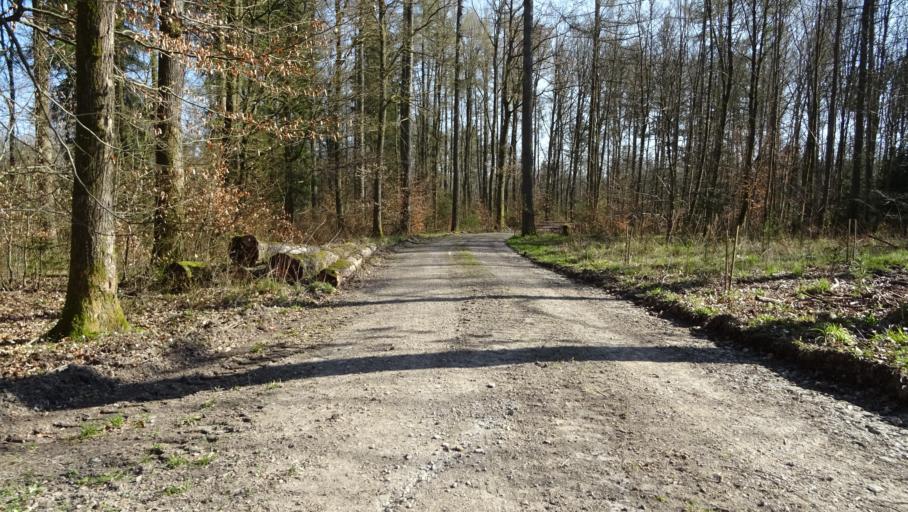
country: DE
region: Baden-Wuerttemberg
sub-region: Regierungsbezirk Stuttgart
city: Roigheim
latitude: 49.3912
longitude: 9.3398
